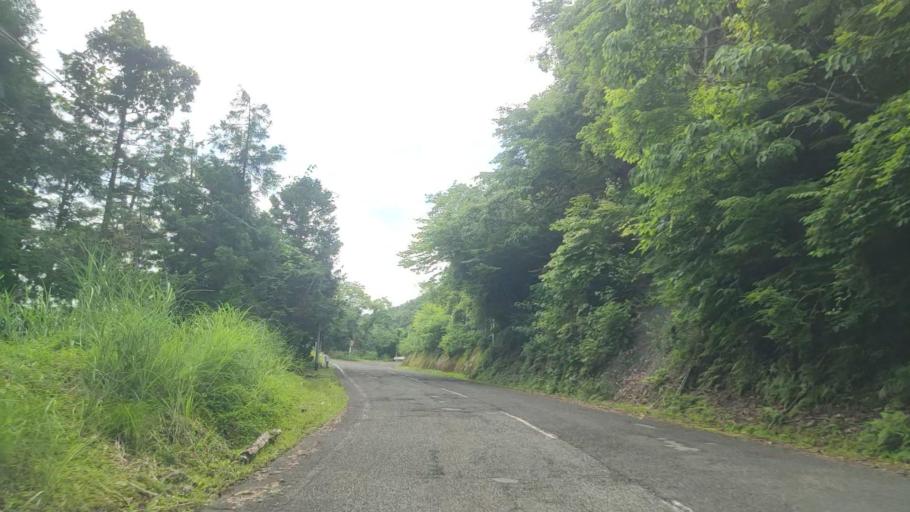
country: JP
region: Hyogo
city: Toyooka
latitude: 35.5182
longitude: 134.6863
